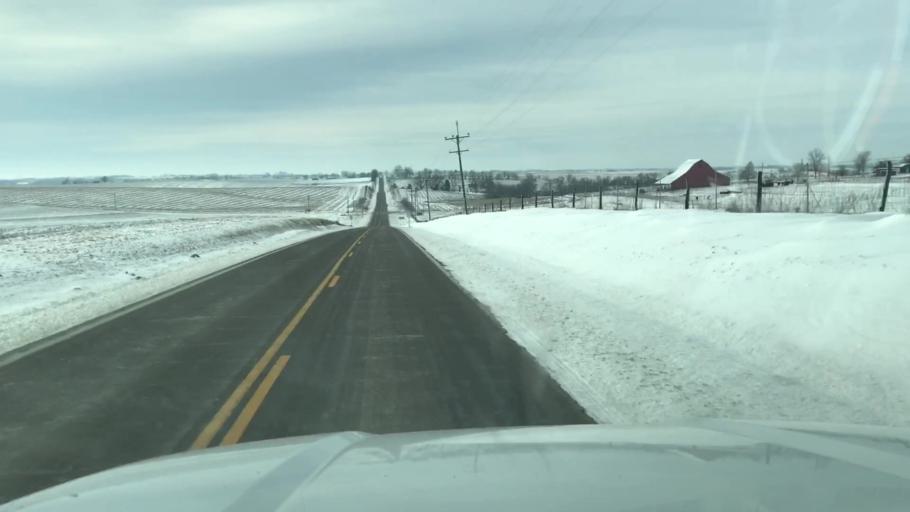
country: US
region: Missouri
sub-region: Holt County
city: Oregon
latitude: 40.0828
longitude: -95.1355
